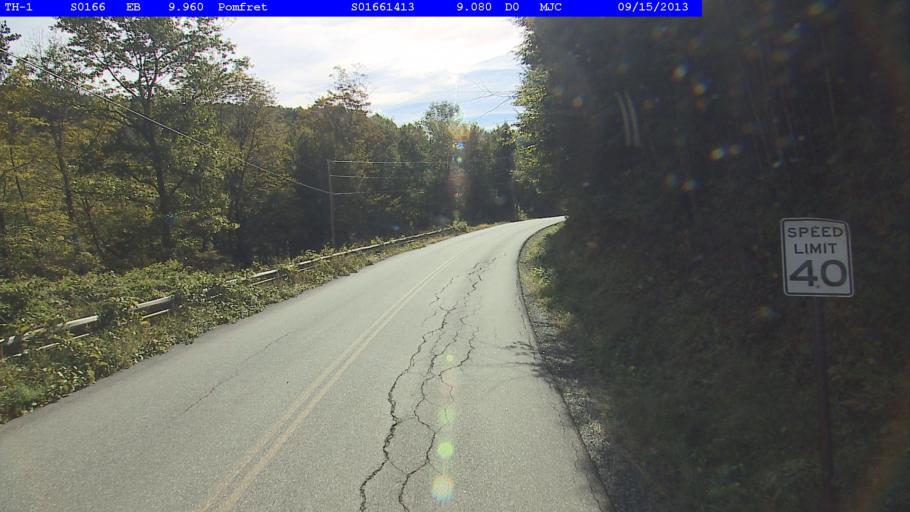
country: US
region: Vermont
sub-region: Windsor County
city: Woodstock
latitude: 43.7240
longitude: -72.4432
